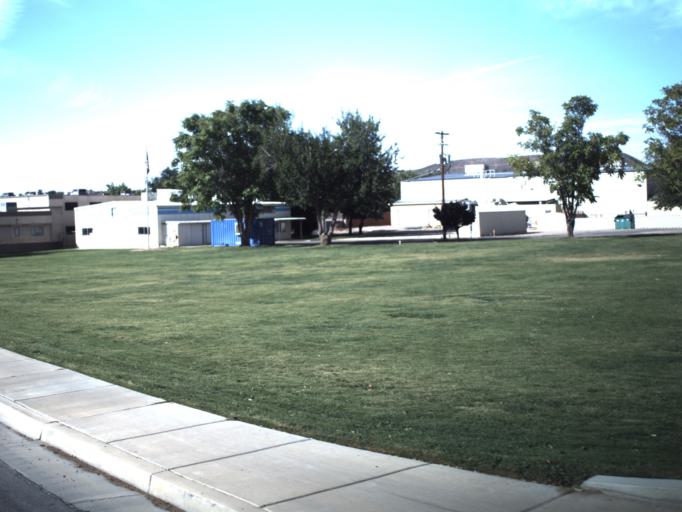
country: US
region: Utah
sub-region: Washington County
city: LaVerkin
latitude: 37.2013
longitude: -113.2726
